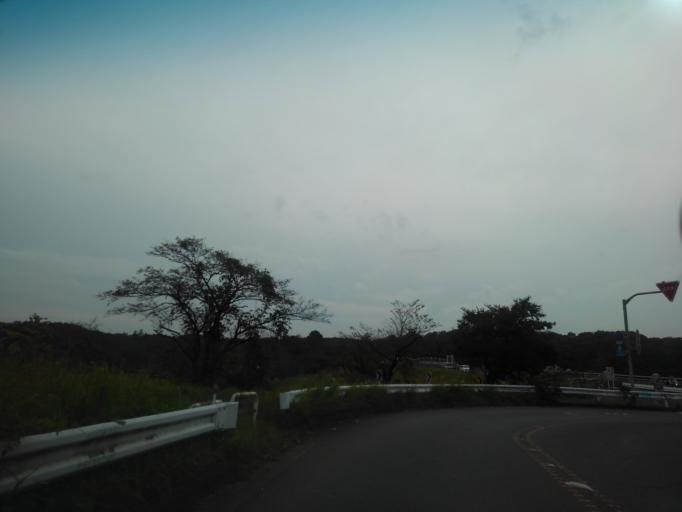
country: JP
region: Tokyo
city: Higashimurayama-shi
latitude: 35.7652
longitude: 139.4177
